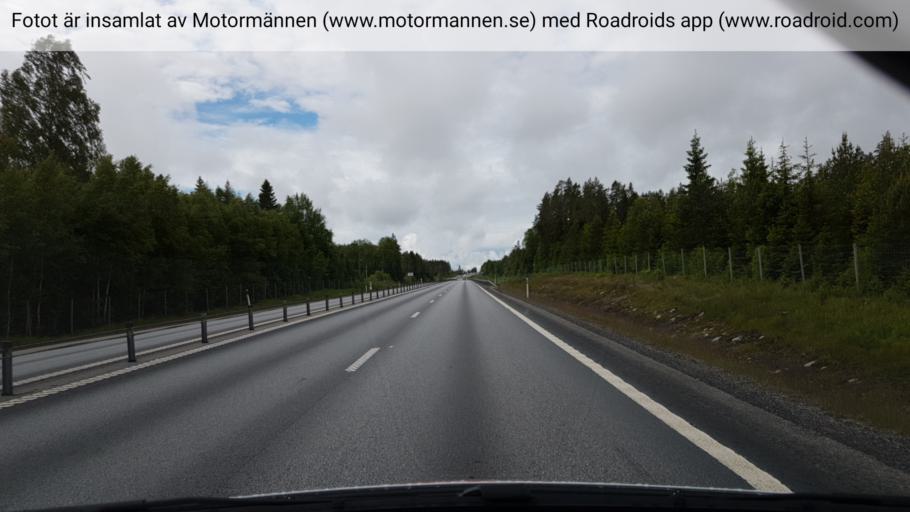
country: SE
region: Vaesterbotten
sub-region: Umea Kommun
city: Hoernefors
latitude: 63.6614
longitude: 19.9626
